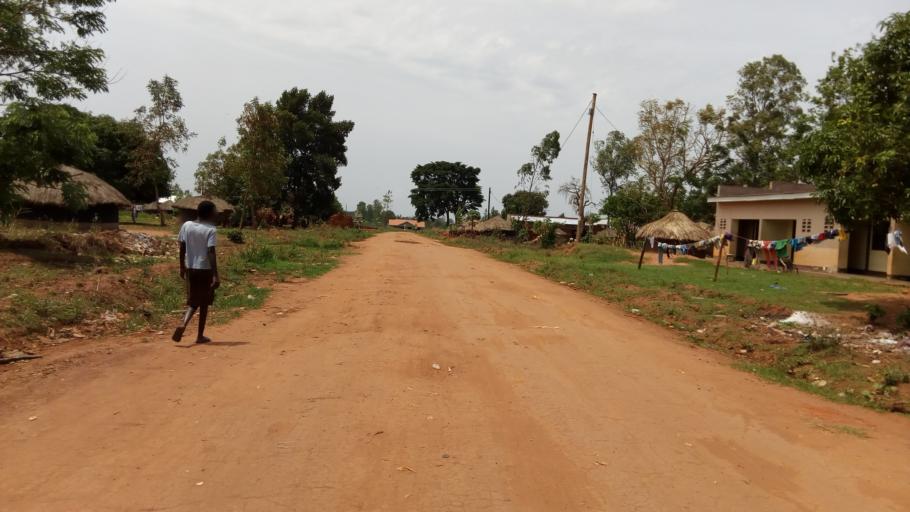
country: UG
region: Northern Region
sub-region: Gulu District
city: Gulu
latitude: 2.7731
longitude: 32.3211
